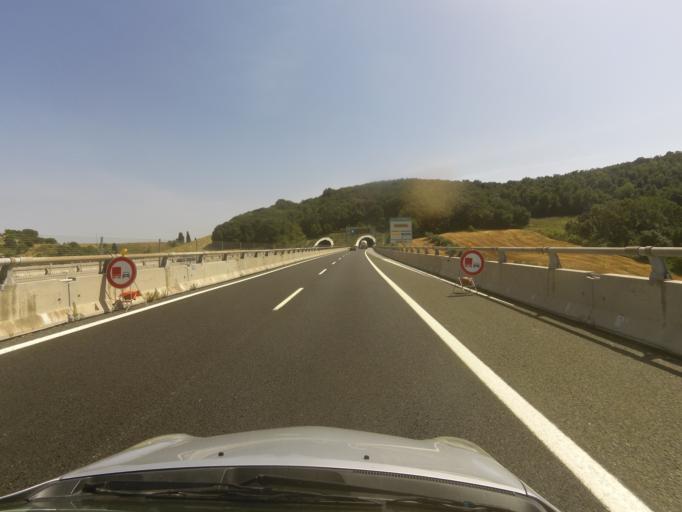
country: IT
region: Tuscany
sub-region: Provincia di Livorno
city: Rosignano Marittimo
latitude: 43.3954
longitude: 10.4934
